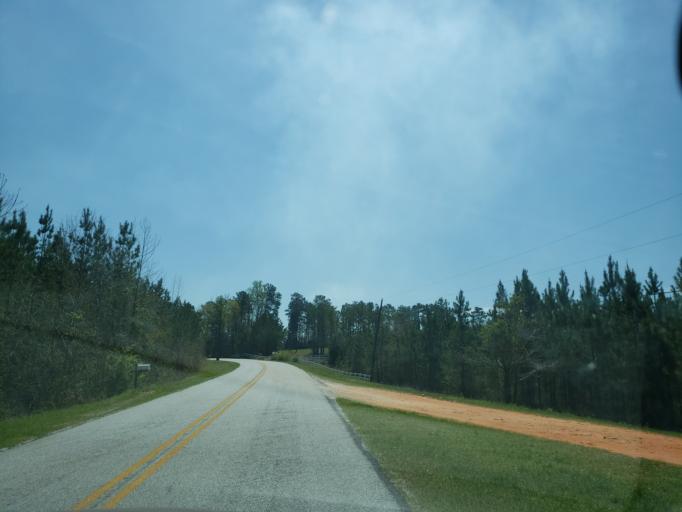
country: US
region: Alabama
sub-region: Elmore County
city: Tallassee
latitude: 32.6689
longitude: -85.8591
